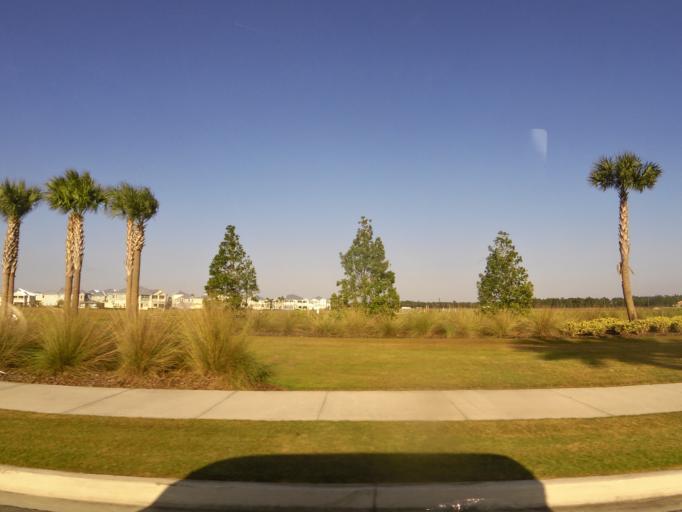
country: US
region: Florida
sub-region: Saint Johns County
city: Palm Valley
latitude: 30.0795
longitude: -81.4874
